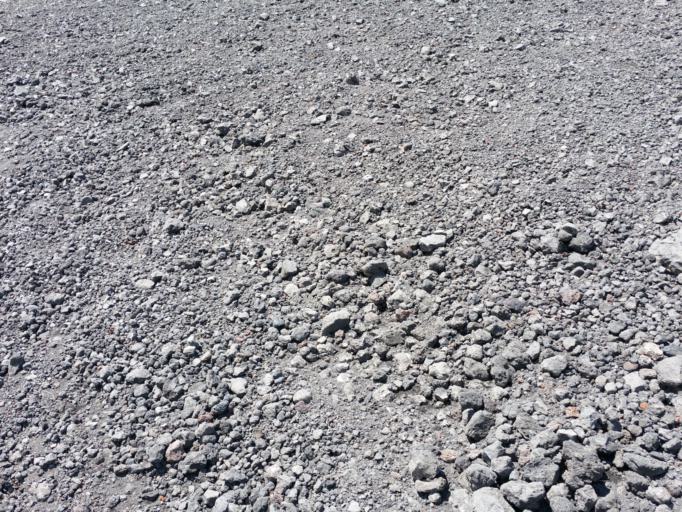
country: IT
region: Sicily
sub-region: Catania
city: Nicolosi
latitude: 37.7216
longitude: 15.0042
